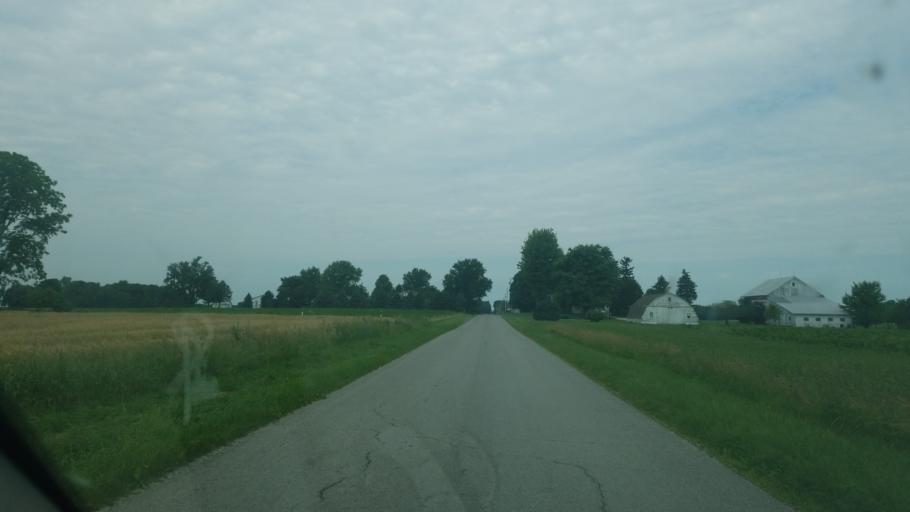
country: US
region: Ohio
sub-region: Seneca County
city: Fostoria
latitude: 41.0502
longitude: -83.4419
